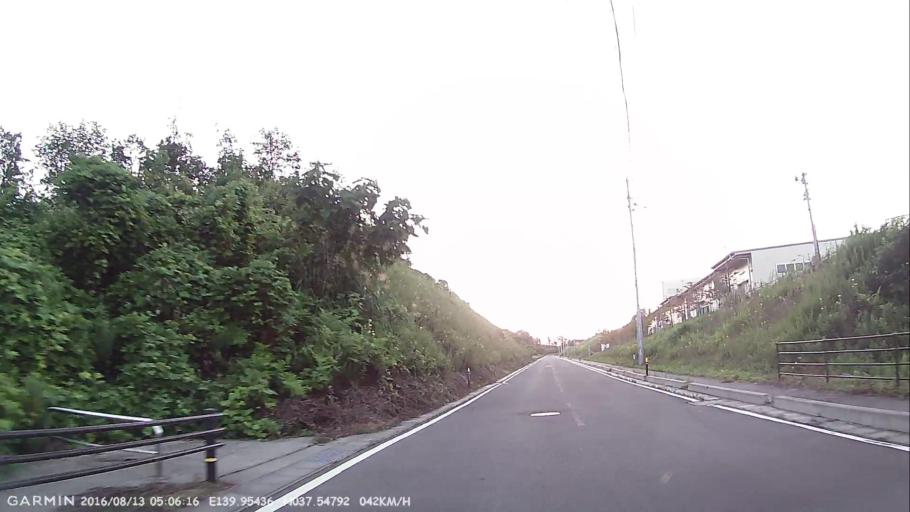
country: JP
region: Fukushima
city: Kitakata
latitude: 37.5479
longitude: 139.9544
